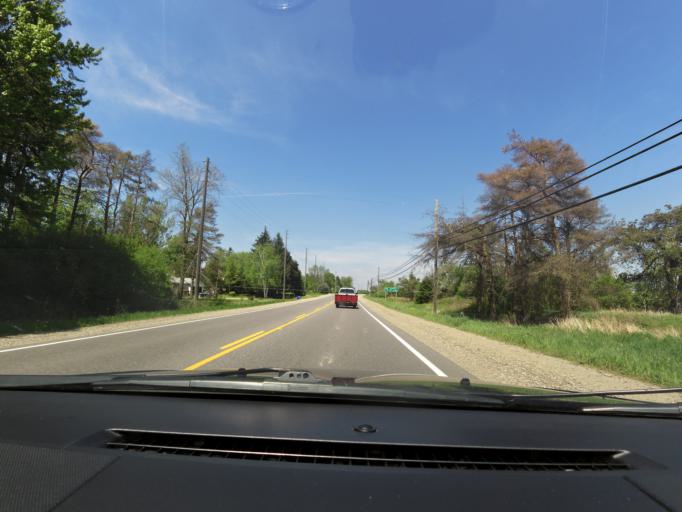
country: CA
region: Ontario
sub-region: Wellington County
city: Guelph
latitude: 43.5980
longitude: -80.1707
